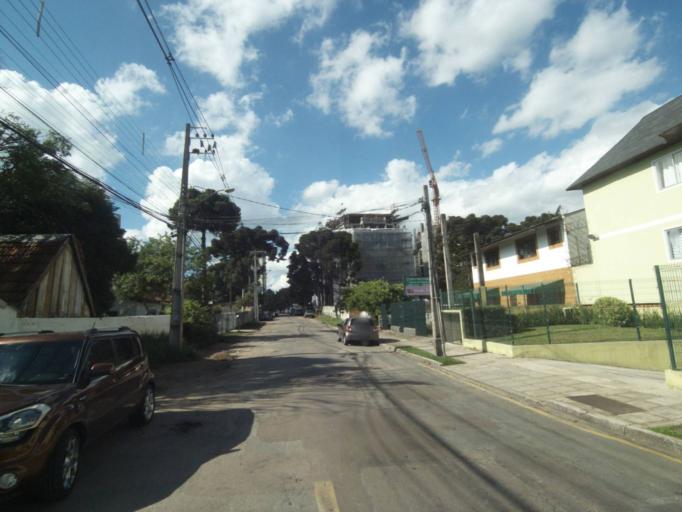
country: BR
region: Parana
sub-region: Curitiba
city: Curitiba
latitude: -25.4439
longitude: -49.3429
